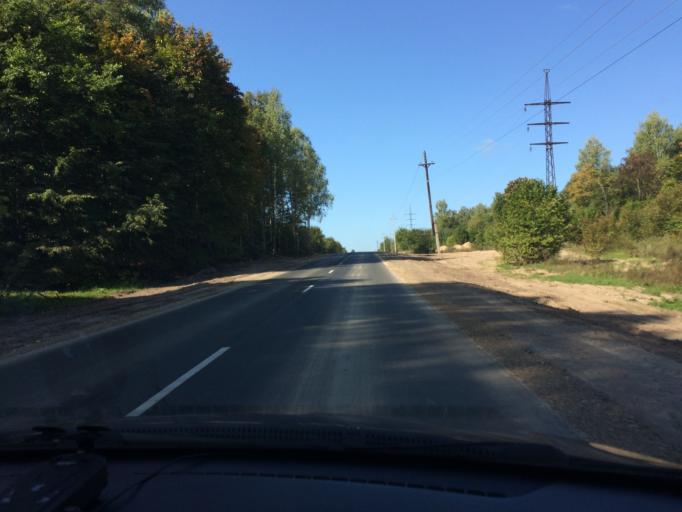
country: RU
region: Mariy-El
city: Sovetskiy
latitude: 56.5461
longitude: 48.4260
